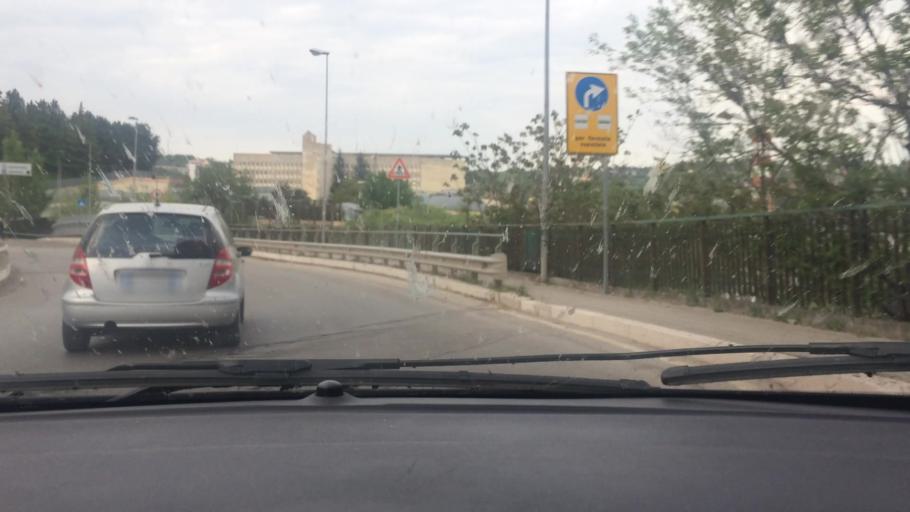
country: IT
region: Basilicate
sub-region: Provincia di Potenza
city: Potenza
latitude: 40.6511
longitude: 15.8014
